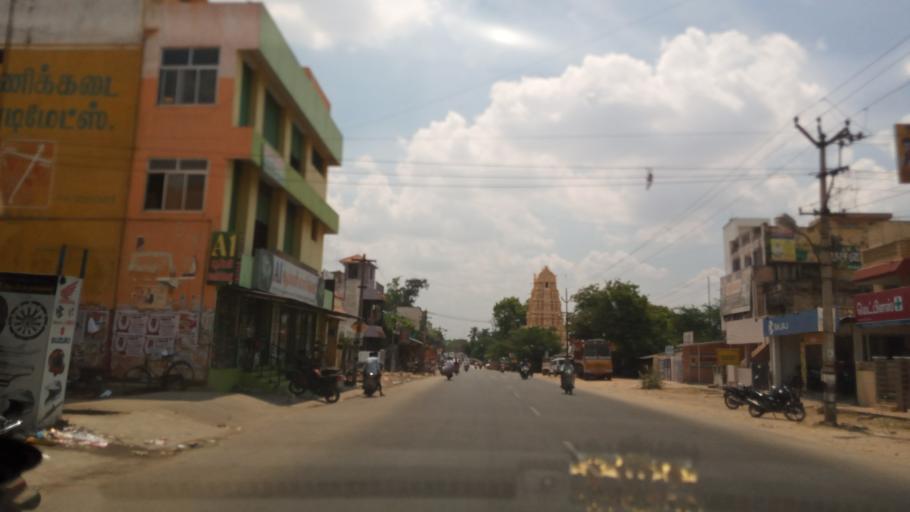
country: IN
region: Tamil Nadu
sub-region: Vellore
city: Walajapet
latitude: 12.9255
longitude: 79.3609
